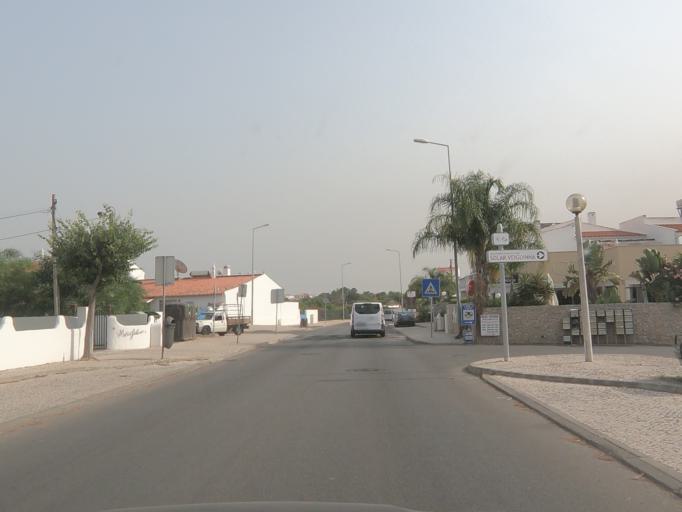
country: PT
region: Faro
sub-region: Albufeira
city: Guia
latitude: 37.0926
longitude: -8.3099
